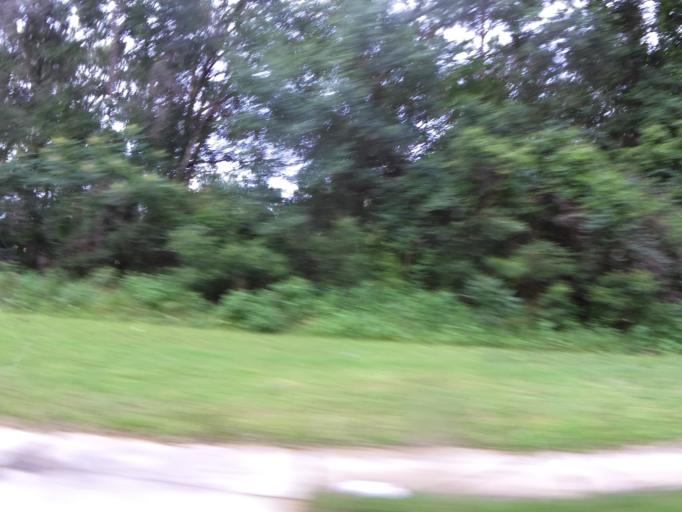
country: US
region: Florida
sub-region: Duval County
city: Jacksonville
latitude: 30.3952
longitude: -81.7147
